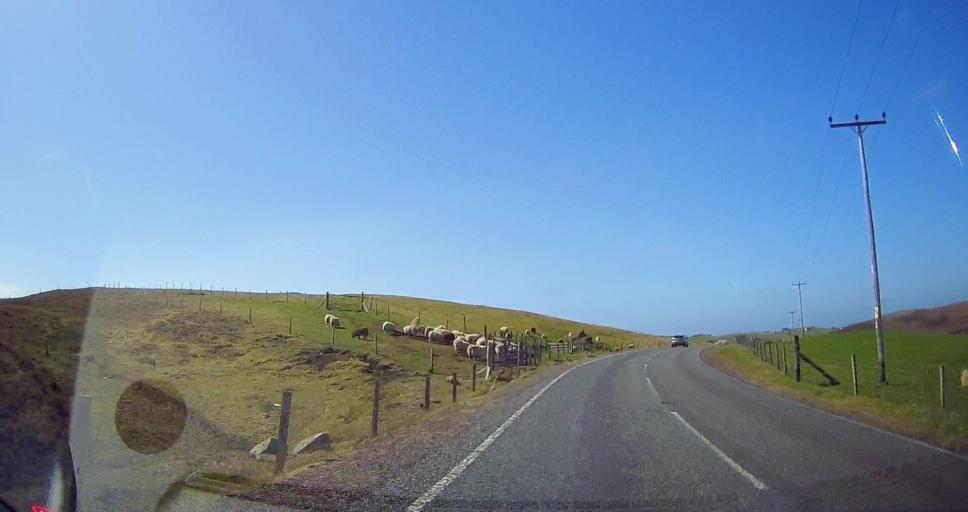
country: GB
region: Scotland
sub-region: Shetland Islands
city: Sandwick
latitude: 60.1071
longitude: -1.2987
